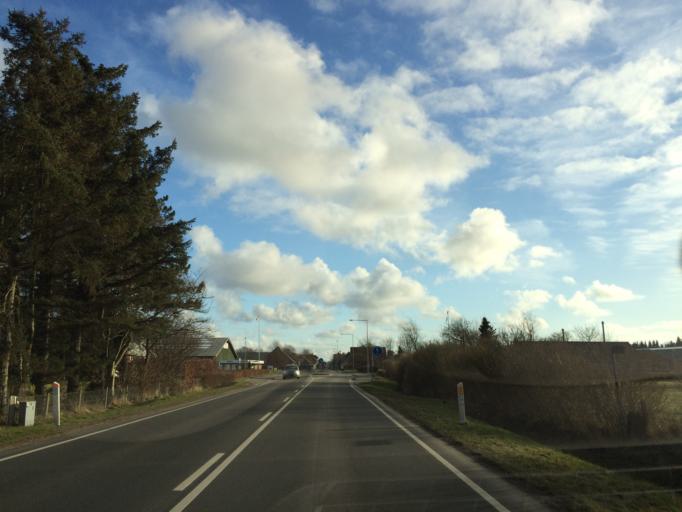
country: DK
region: Central Jutland
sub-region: Holstebro Kommune
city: Ulfborg
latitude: 56.3483
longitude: 8.3411
